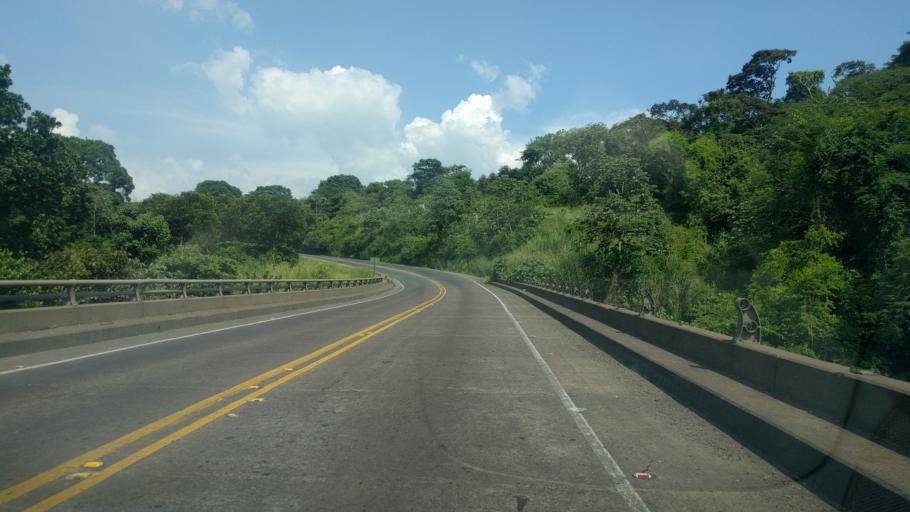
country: CR
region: Alajuela
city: Carrillos
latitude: 10.0180
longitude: -84.3347
